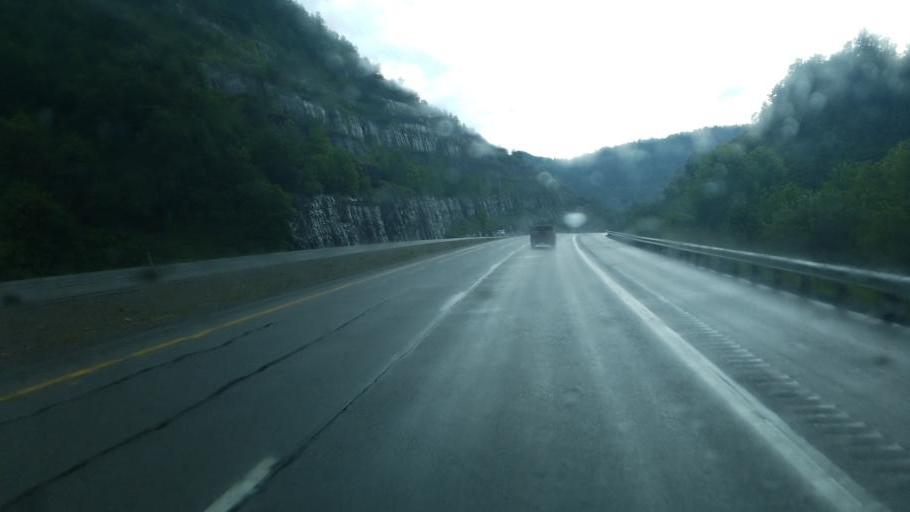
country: US
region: Kentucky
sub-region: Pike County
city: Pikeville
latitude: 37.5305
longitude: -82.4504
